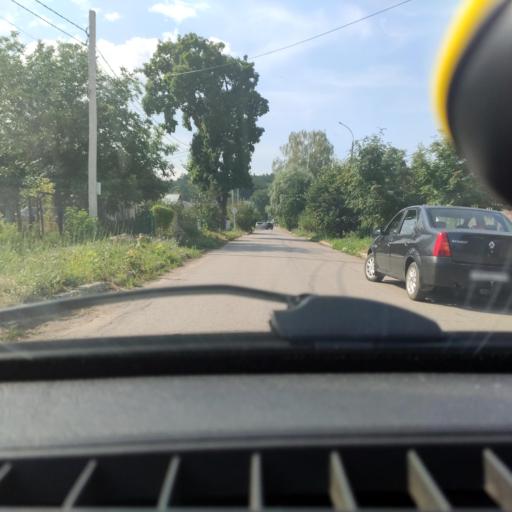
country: RU
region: Samara
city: Zhigulevsk
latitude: 53.4045
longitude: 49.4832
